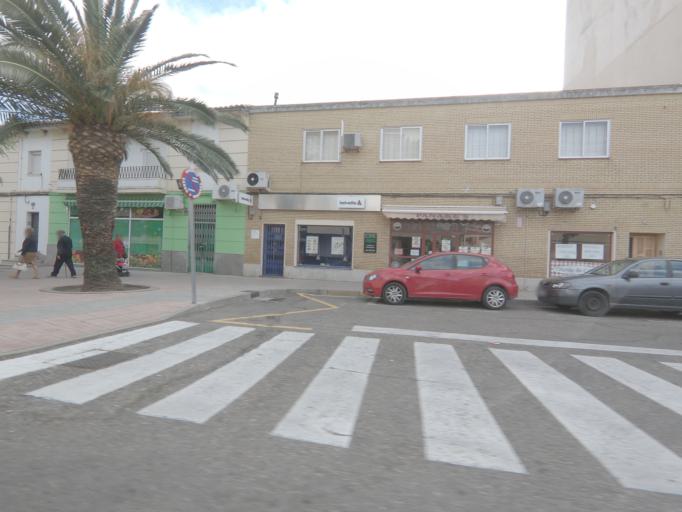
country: ES
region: Extremadura
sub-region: Provincia de Caceres
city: Coria
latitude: 39.9898
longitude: -6.5393
